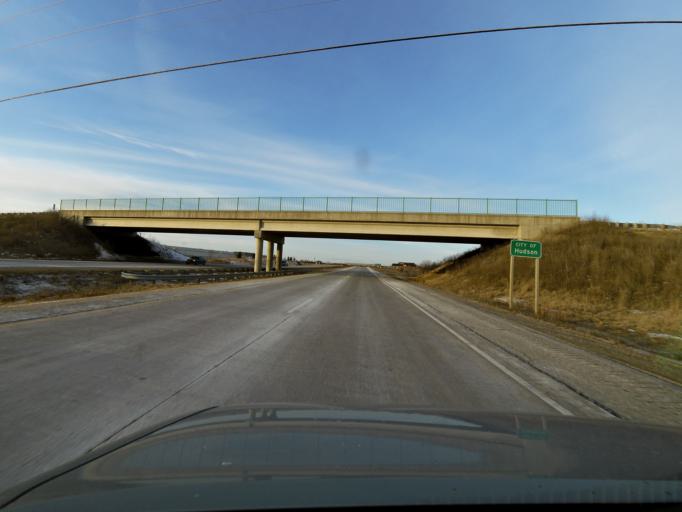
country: US
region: Wisconsin
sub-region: Saint Croix County
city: Hudson
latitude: 44.9416
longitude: -92.6937
